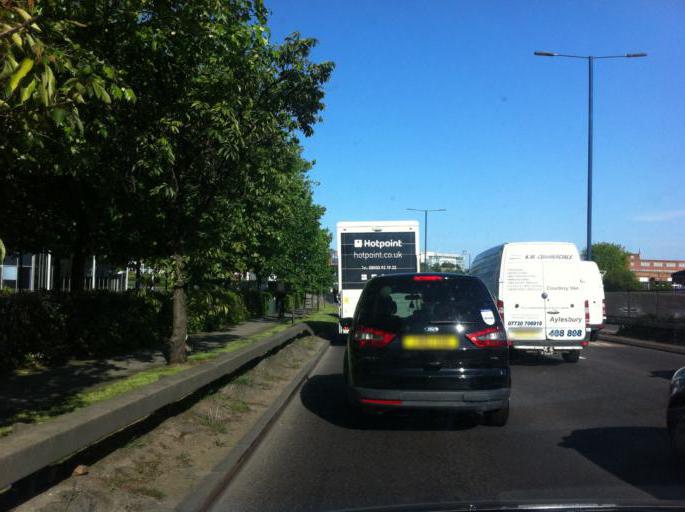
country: GB
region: England
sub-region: Greater London
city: Acton
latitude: 51.5257
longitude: -0.2726
